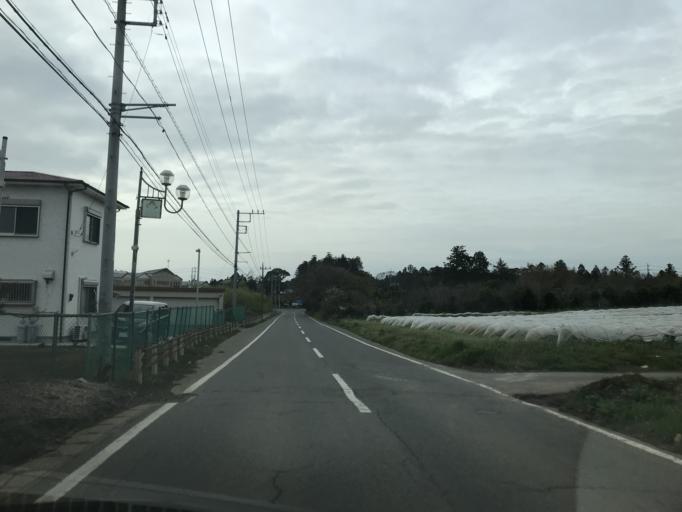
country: JP
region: Chiba
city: Omigawa
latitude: 35.8014
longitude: 140.5785
